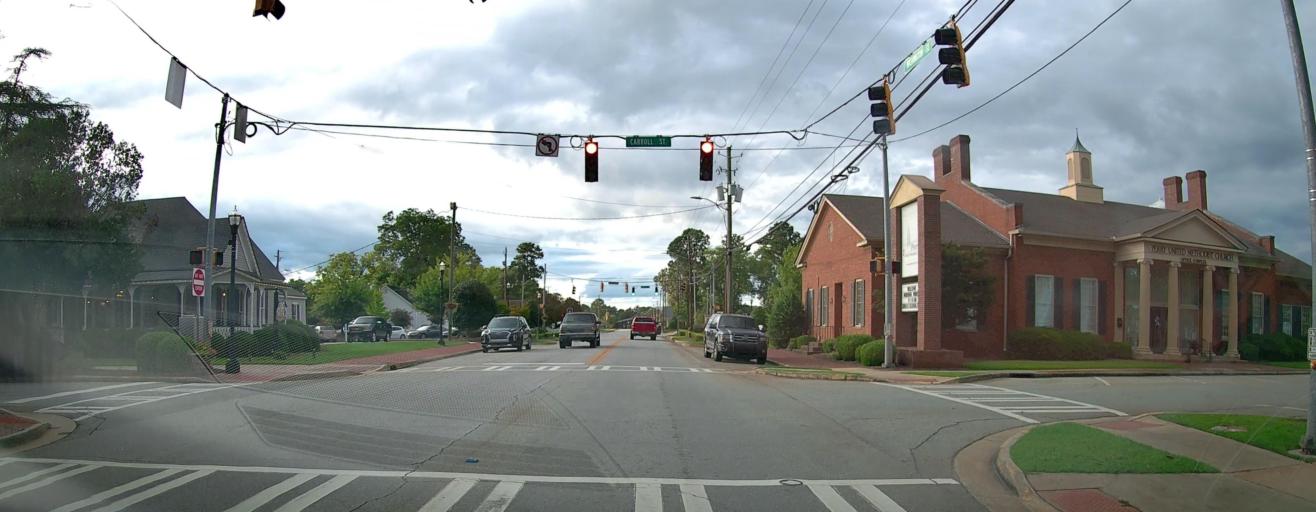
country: US
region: Georgia
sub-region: Houston County
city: Perry
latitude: 32.4586
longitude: -83.7321
